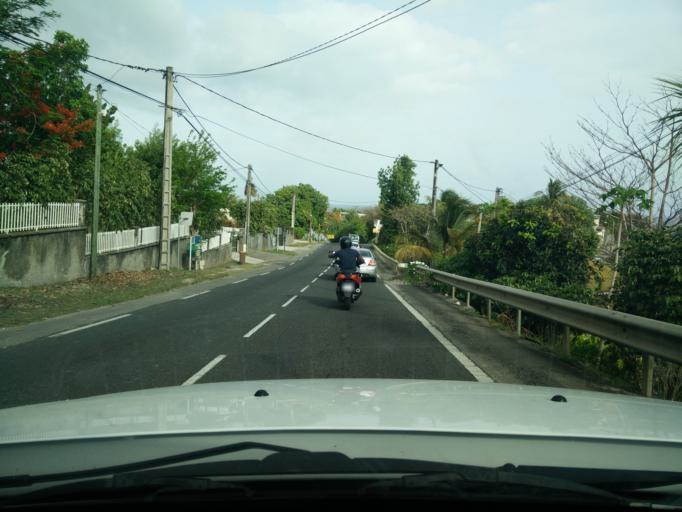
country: GP
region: Guadeloupe
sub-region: Guadeloupe
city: Sainte-Anne
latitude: 16.2140
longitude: -61.4285
